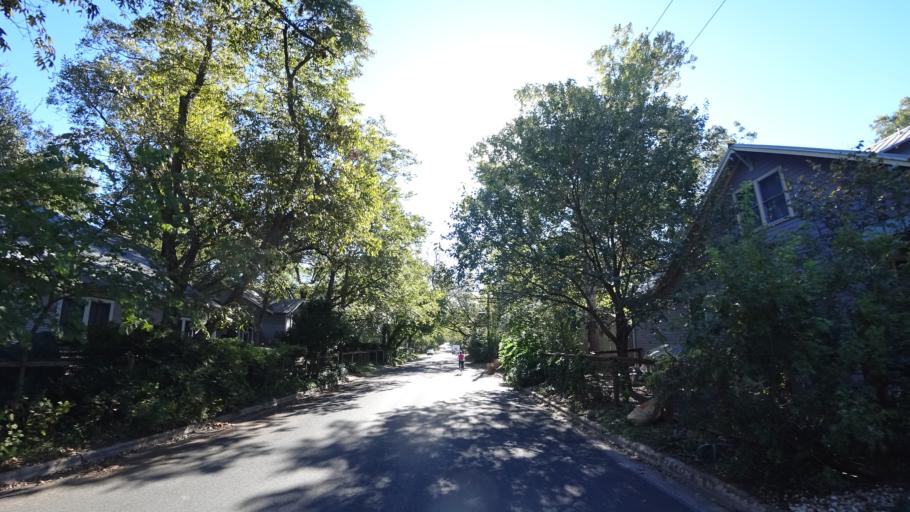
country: US
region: Texas
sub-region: Travis County
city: Austin
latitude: 30.3119
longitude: -97.7298
